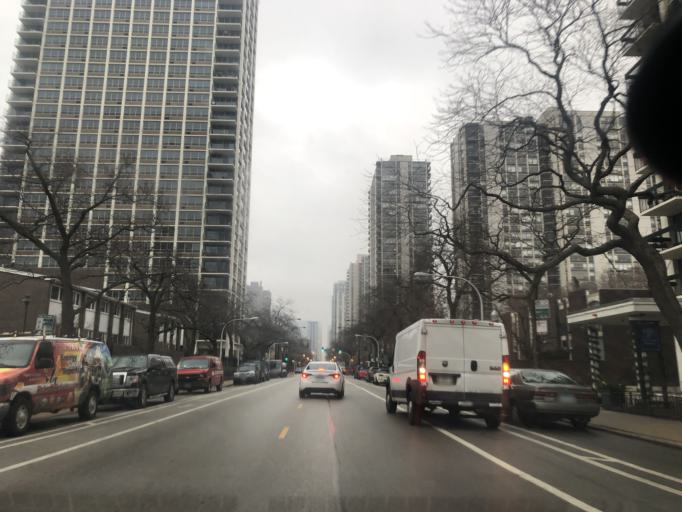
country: US
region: Illinois
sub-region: Cook County
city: Chicago
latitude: 41.9091
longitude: -87.6316
